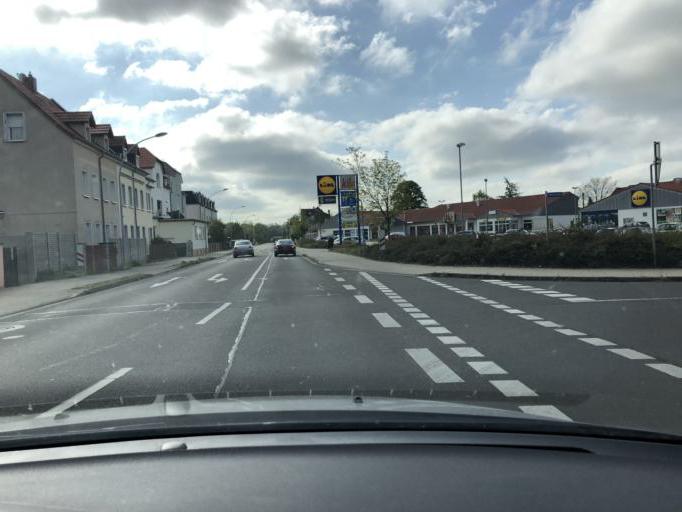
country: DE
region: Saxony
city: Bohlen
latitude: 51.1997
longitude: 12.3908
